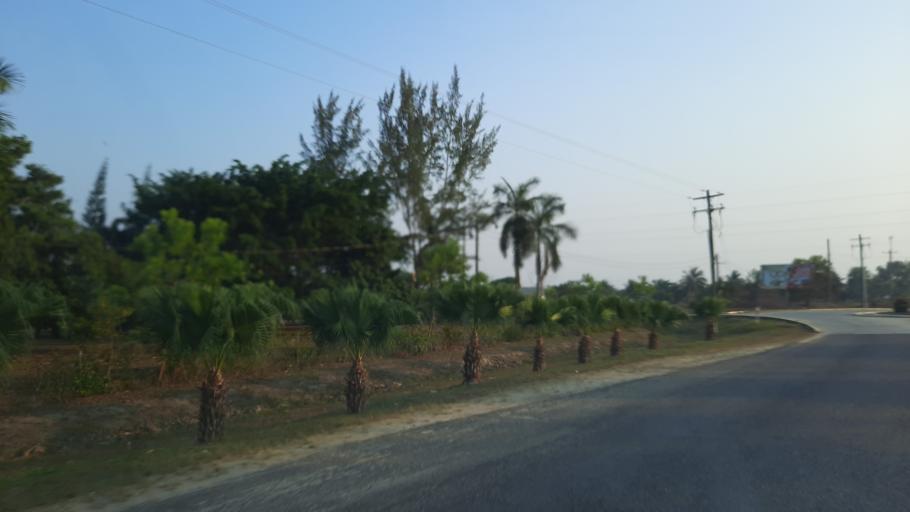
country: BZ
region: Stann Creek
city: Placencia
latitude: 16.7067
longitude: -88.4241
